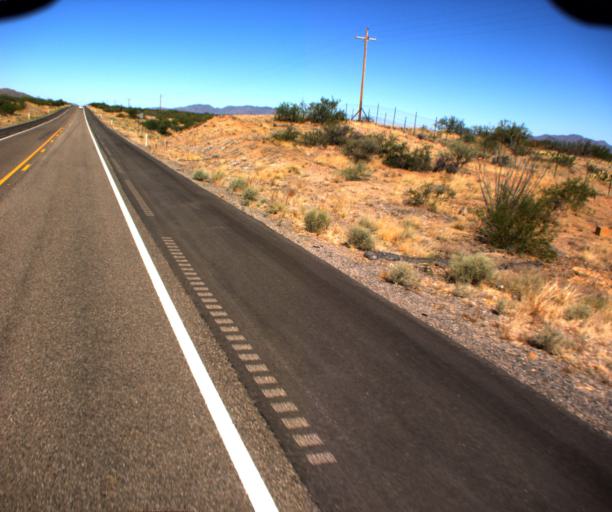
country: US
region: Arizona
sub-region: Pima County
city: Three Points
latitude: 32.0240
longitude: -111.5924
